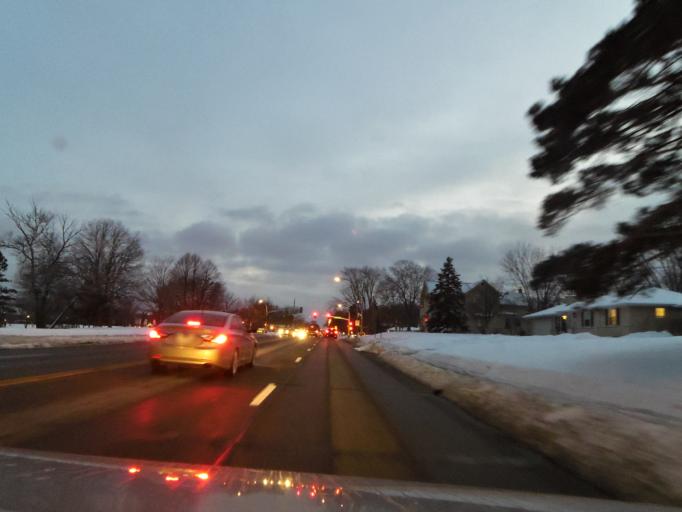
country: US
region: Minnesota
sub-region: Hennepin County
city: Richfield
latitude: 44.8883
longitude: -93.2679
